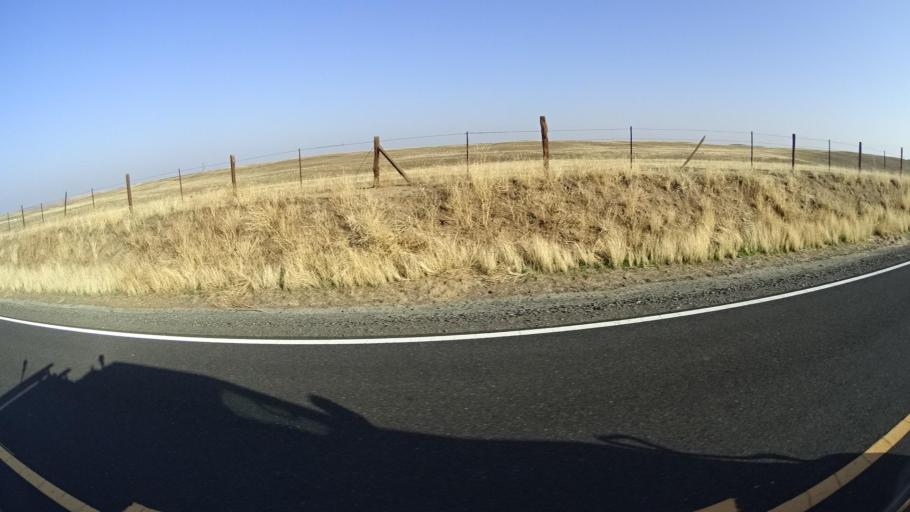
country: US
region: California
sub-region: Tulare County
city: Richgrove
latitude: 35.7510
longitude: -119.0036
